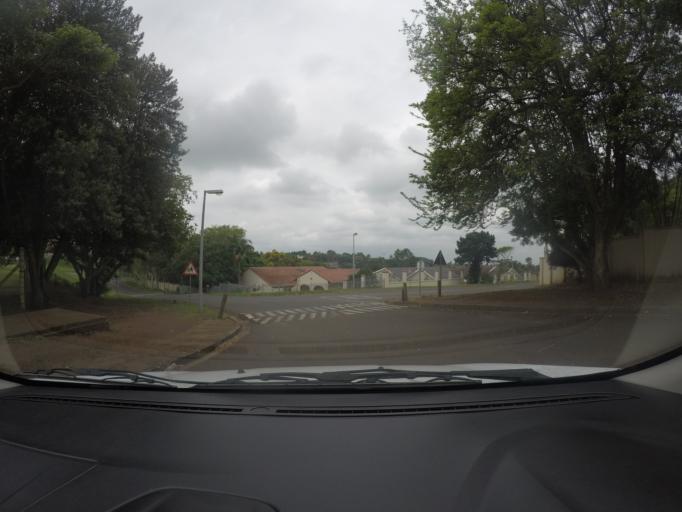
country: ZA
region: KwaZulu-Natal
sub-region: uThungulu District Municipality
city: Empangeni
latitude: -28.7529
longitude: 31.8861
